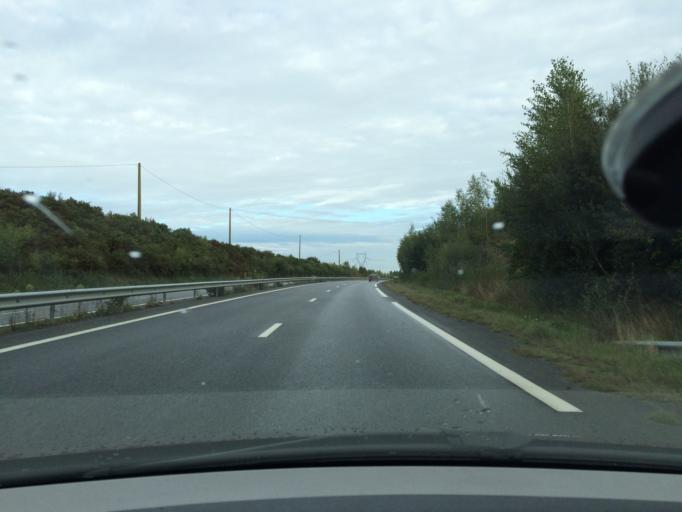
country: FR
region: Brittany
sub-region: Departement d'Ille-et-Vilaine
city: Janze
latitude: 47.9577
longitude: -1.5174
